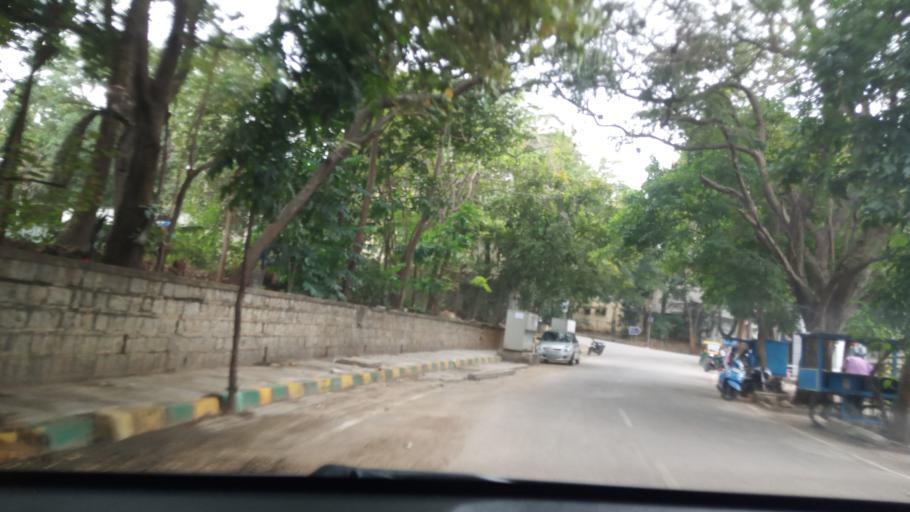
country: IN
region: Karnataka
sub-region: Bangalore Urban
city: Bangalore
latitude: 13.0113
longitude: 77.5379
